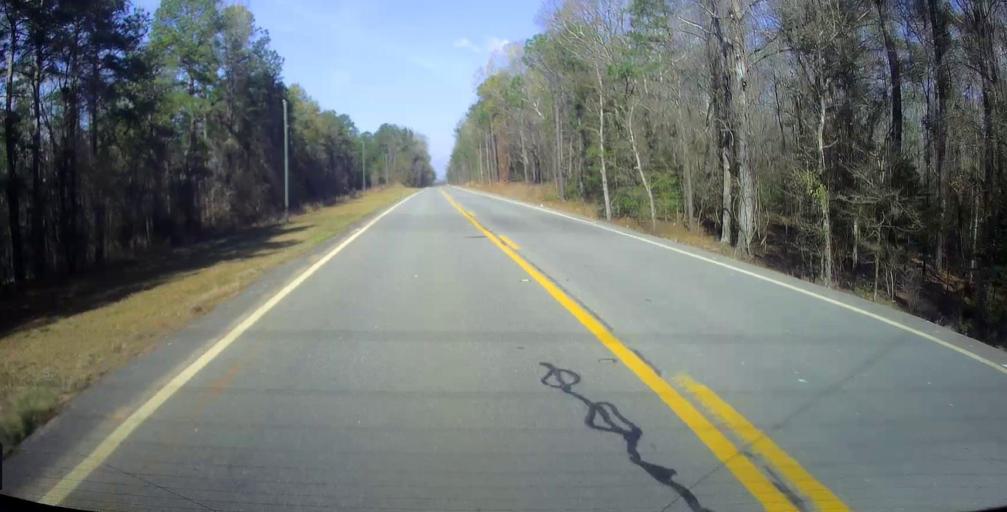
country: US
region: Georgia
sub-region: Wilkinson County
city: Gordon
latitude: 32.8045
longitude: -83.3272
